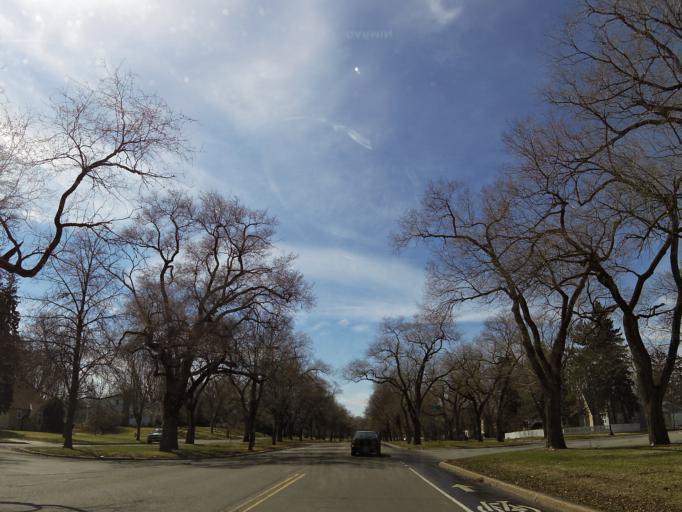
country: US
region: Minnesota
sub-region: Ramsey County
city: Saint Paul
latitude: 44.9562
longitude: -93.0465
